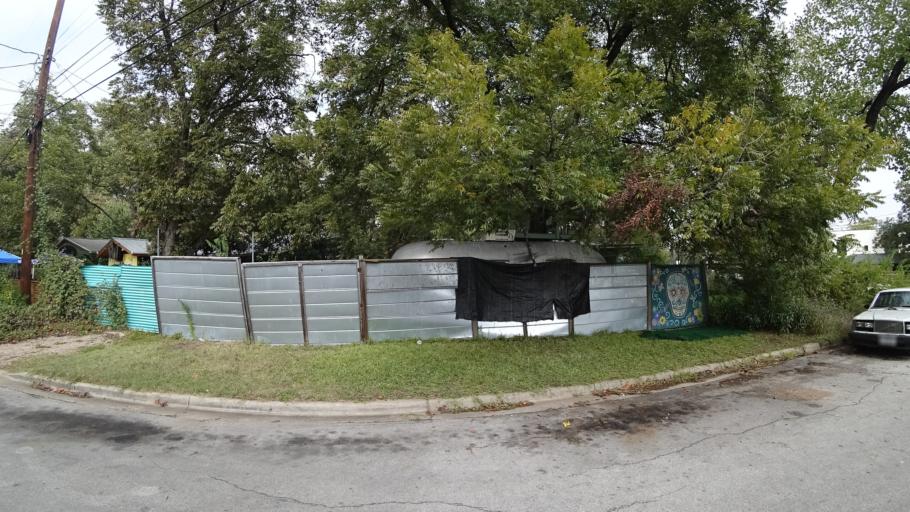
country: US
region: Texas
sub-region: Travis County
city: Rollingwood
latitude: 30.2539
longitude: -97.7729
